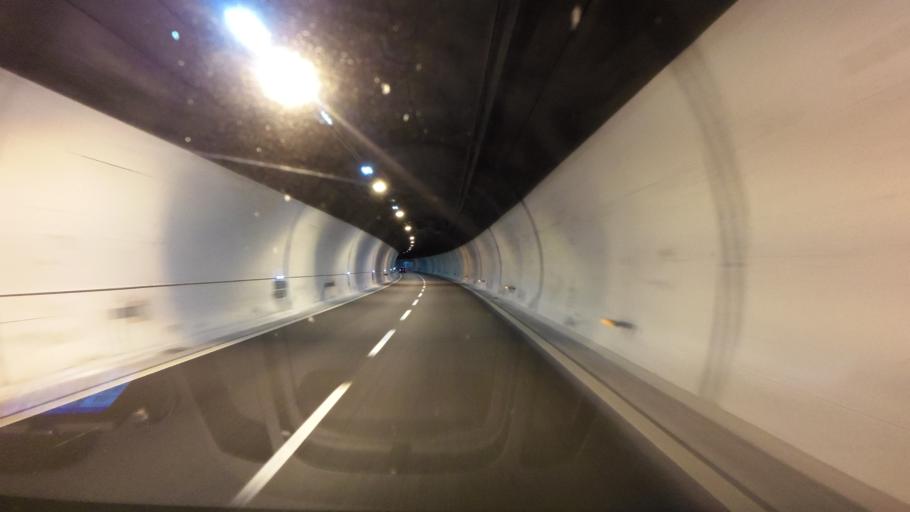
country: IT
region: Friuli Venezia Giulia
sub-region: Provincia di Udine
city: Chiusaforte
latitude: 46.4076
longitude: 13.3172
